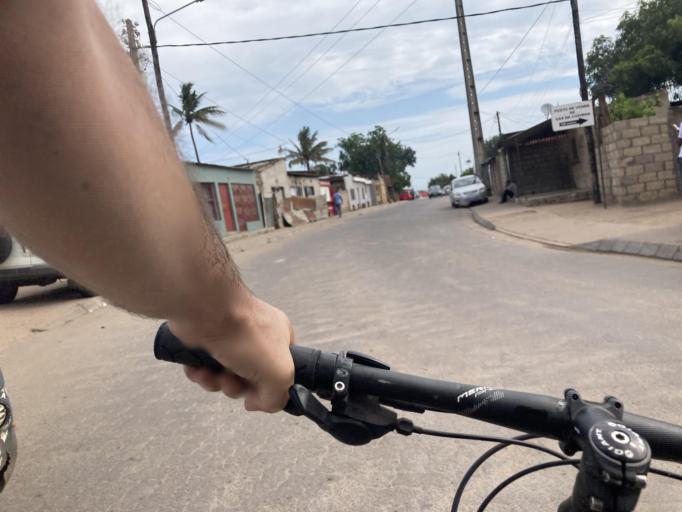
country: MZ
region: Maputo City
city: Maputo
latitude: -25.9332
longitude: 32.5856
